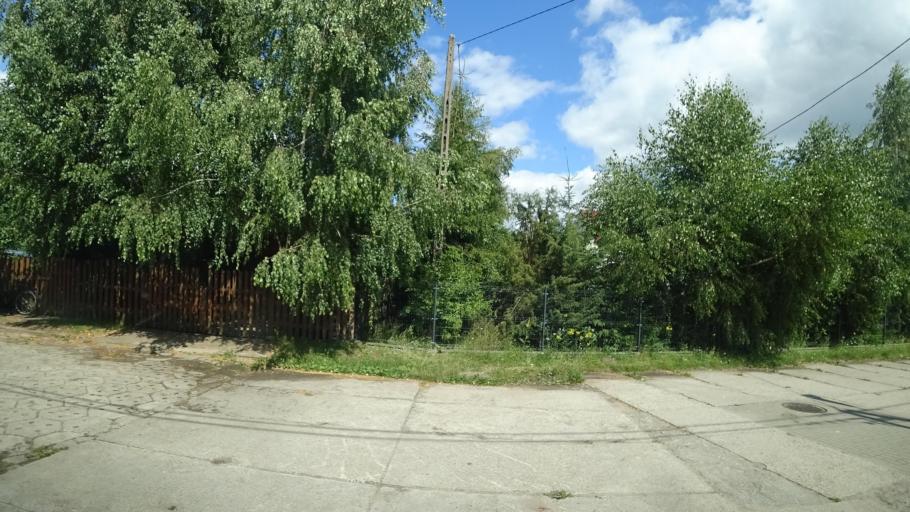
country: PL
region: Warmian-Masurian Voivodeship
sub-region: Powiat goldapski
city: Banie Mazurskie
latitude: 54.2184
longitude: 22.1552
